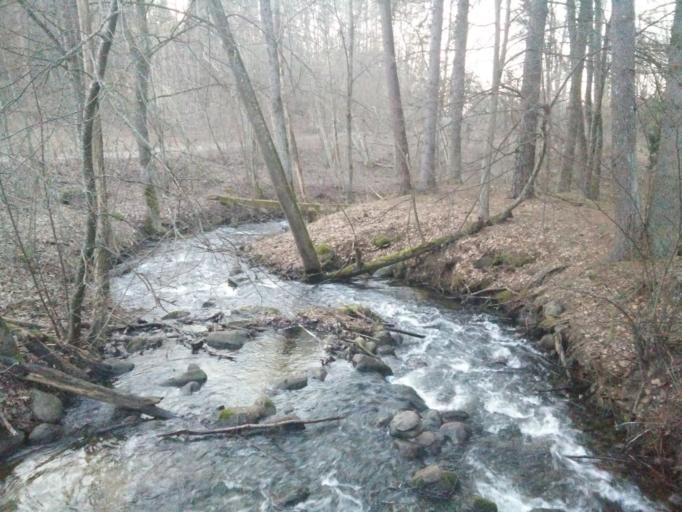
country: LT
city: Grigiskes
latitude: 54.7200
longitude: 25.0433
